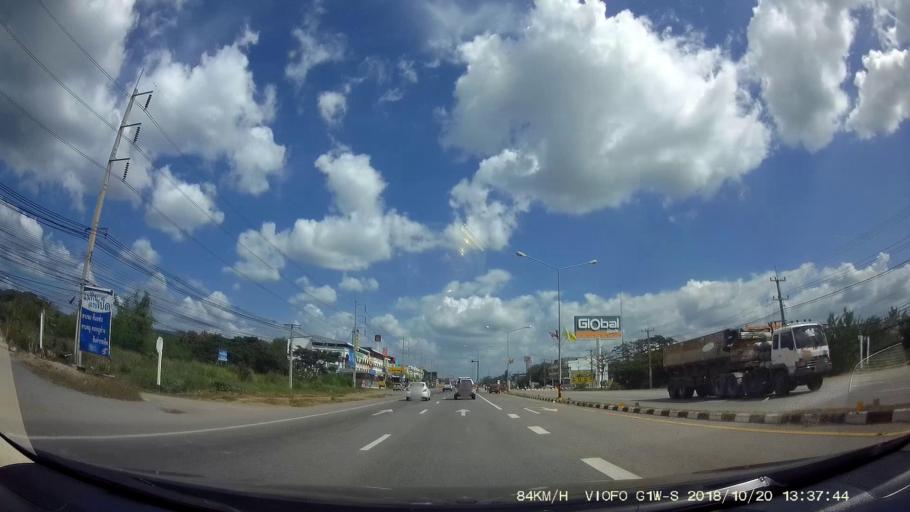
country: TH
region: Khon Kaen
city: Chum Phae
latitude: 16.5564
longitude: 102.0746
